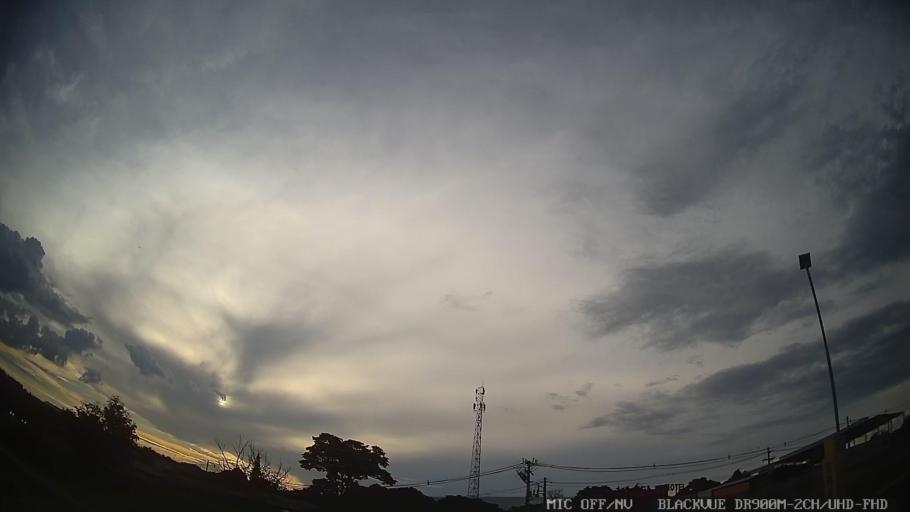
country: BR
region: Sao Paulo
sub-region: Jaguariuna
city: Jaguariuna
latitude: -22.6943
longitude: -47.0127
